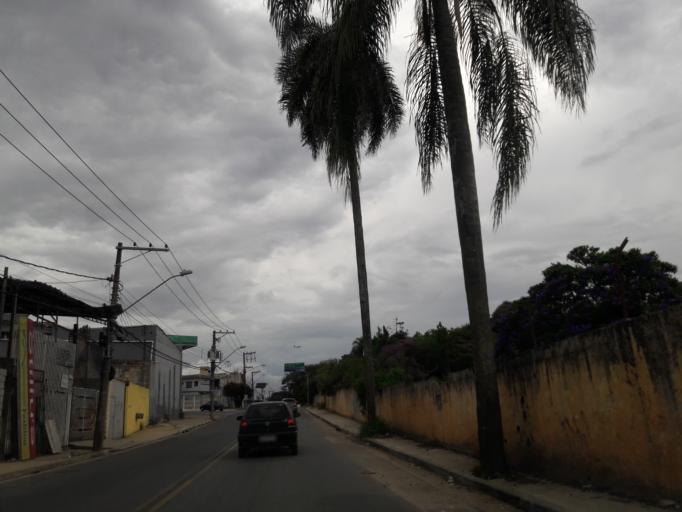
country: BR
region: Sao Paulo
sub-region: Aruja
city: Aruja
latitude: -23.4023
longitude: -46.4055
